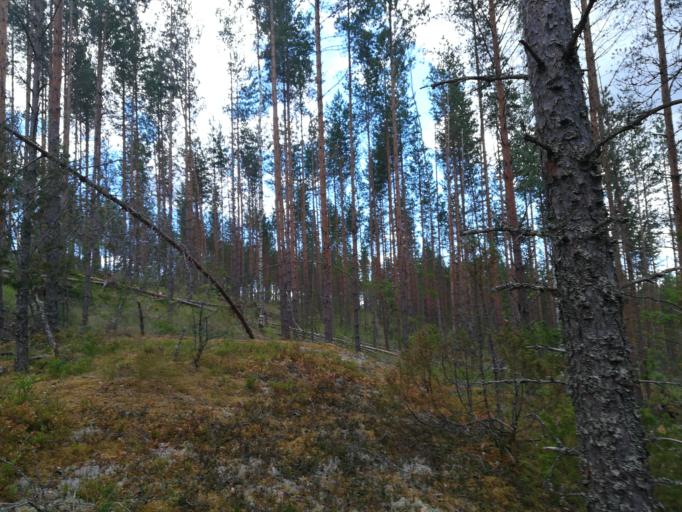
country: FI
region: Southern Savonia
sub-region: Mikkeli
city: Hirvensalmi
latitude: 61.7065
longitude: 26.9717
